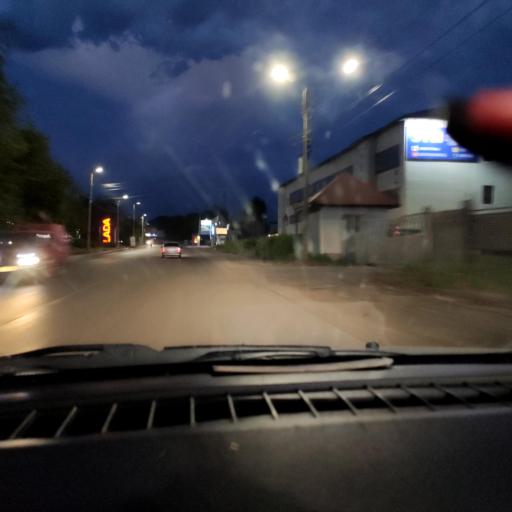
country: RU
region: Orenburg
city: Orenburg
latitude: 51.7999
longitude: 55.1466
